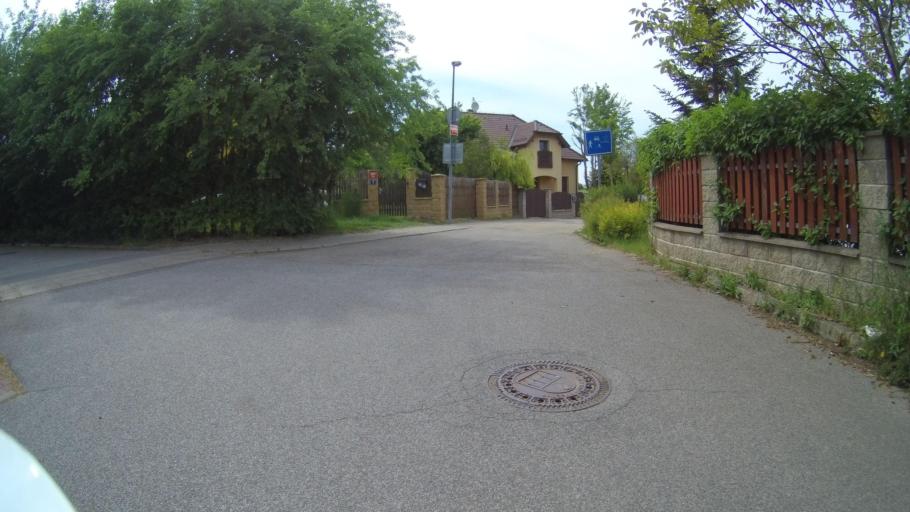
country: CZ
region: Praha
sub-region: Praha 9
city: Strizkov
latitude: 50.1433
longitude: 14.4709
